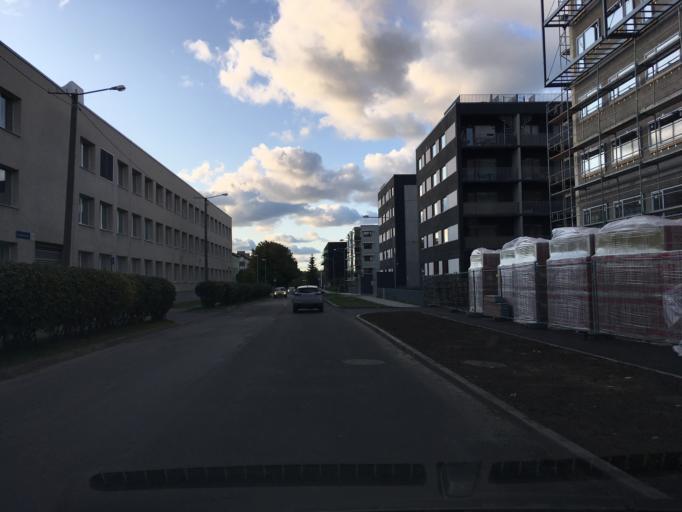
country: EE
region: Harju
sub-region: Tallinna linn
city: Tallinn
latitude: 59.4370
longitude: 24.8075
